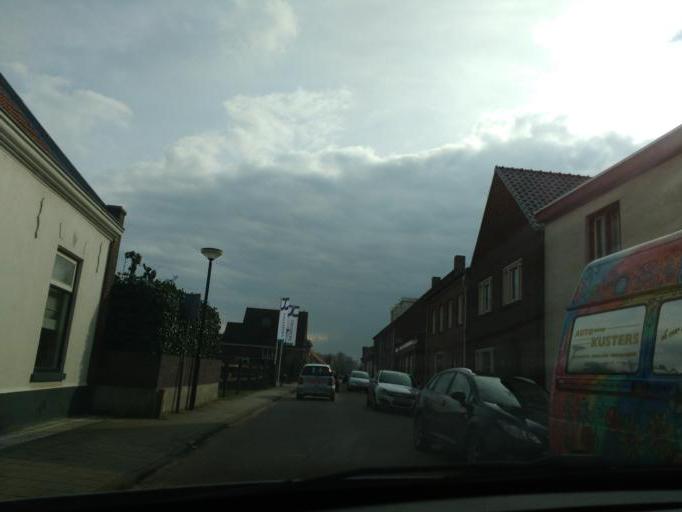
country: NL
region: North Brabant
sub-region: Gemeente Boxmeer
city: Overloon
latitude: 51.5984
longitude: 6.0114
